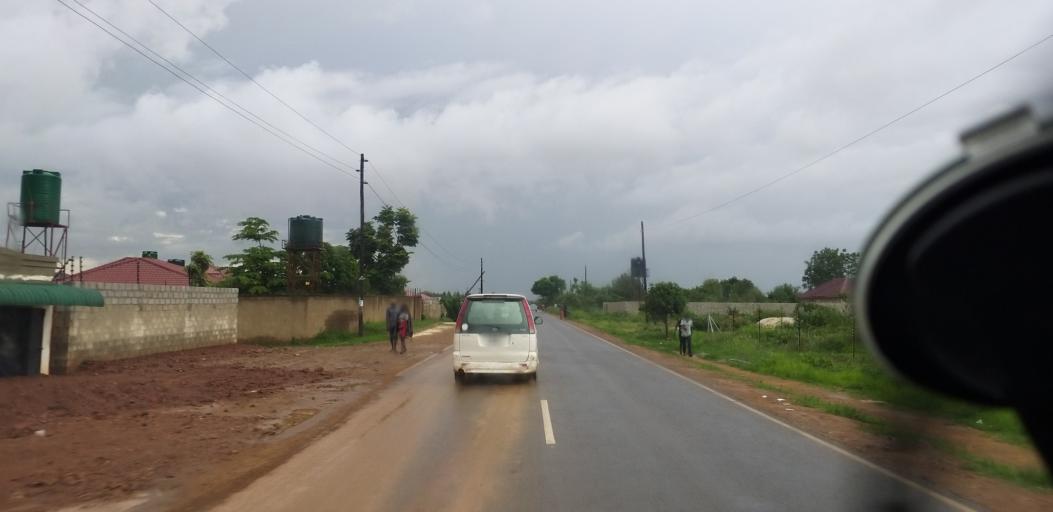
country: ZM
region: Lusaka
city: Lusaka
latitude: -15.4832
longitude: 28.3152
